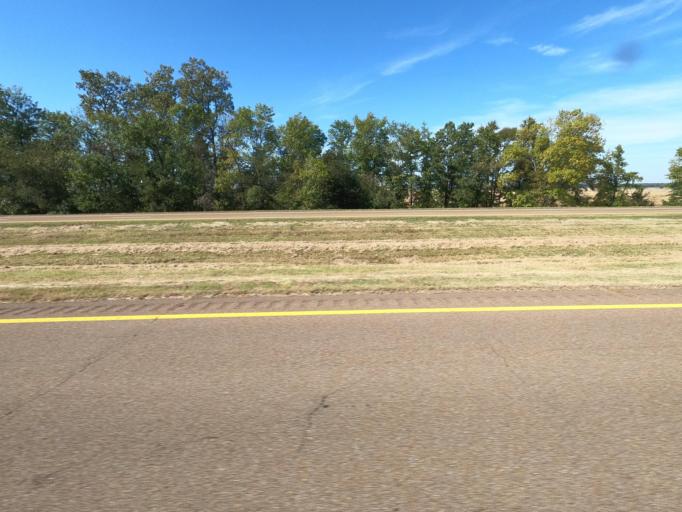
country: US
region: Tennessee
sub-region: Obion County
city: Obion
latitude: 36.1909
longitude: -89.2165
